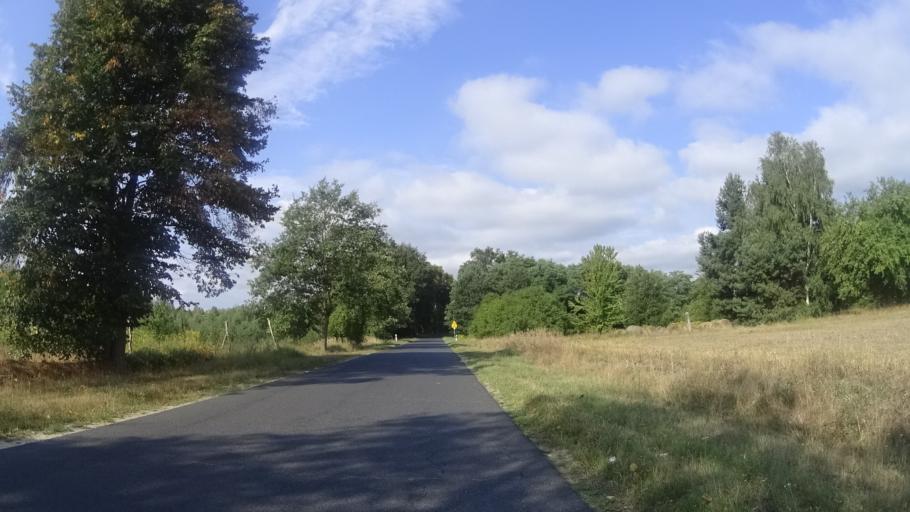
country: PL
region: Lubusz
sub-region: Powiat zarski
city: Przewoz
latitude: 51.4860
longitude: 14.9067
